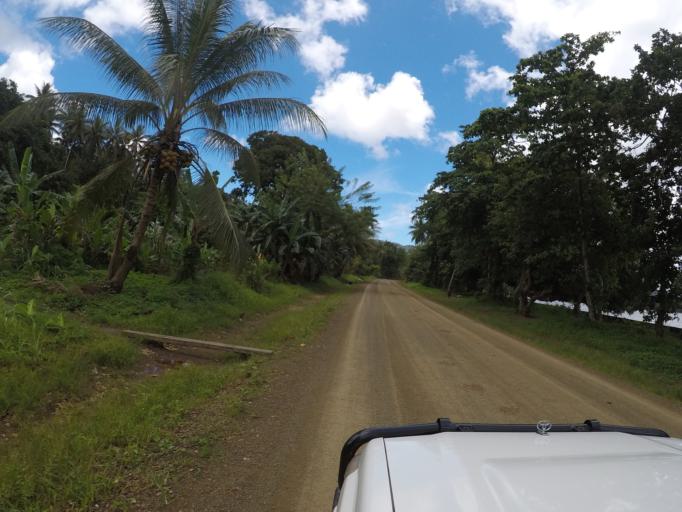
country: PG
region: Milne Bay
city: Alotau
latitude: -10.3360
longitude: 150.6480
